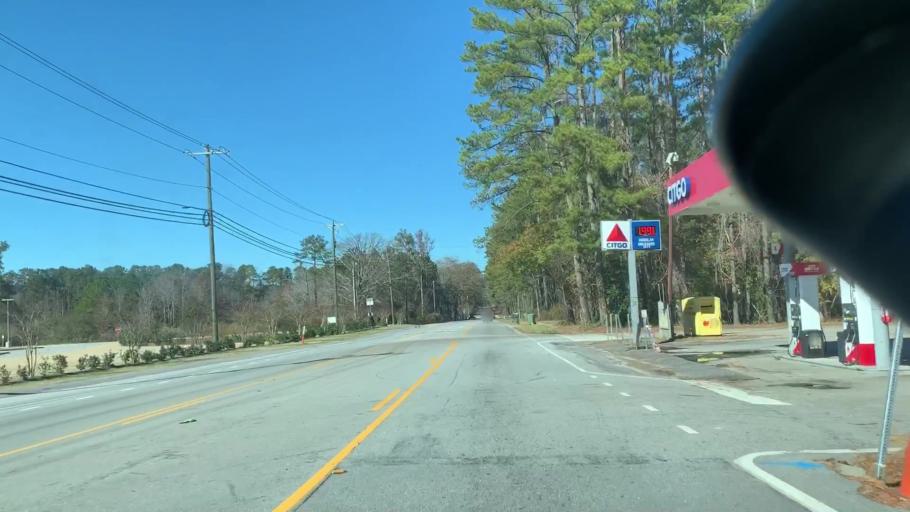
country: US
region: South Carolina
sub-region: Richland County
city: Woodfield
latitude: 34.0765
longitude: -80.9192
